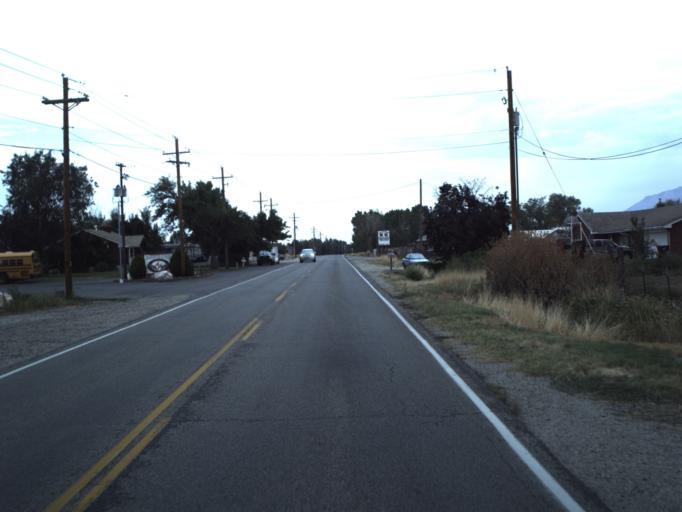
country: US
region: Utah
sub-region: Weber County
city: Hooper
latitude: 41.1946
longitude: -112.0931
